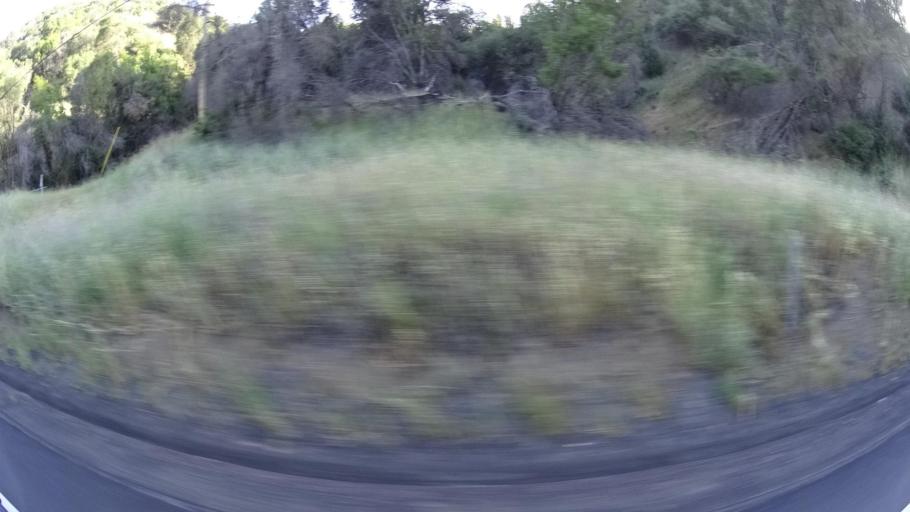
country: US
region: California
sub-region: Lake County
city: Upper Lake
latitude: 39.1662
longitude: -122.9707
